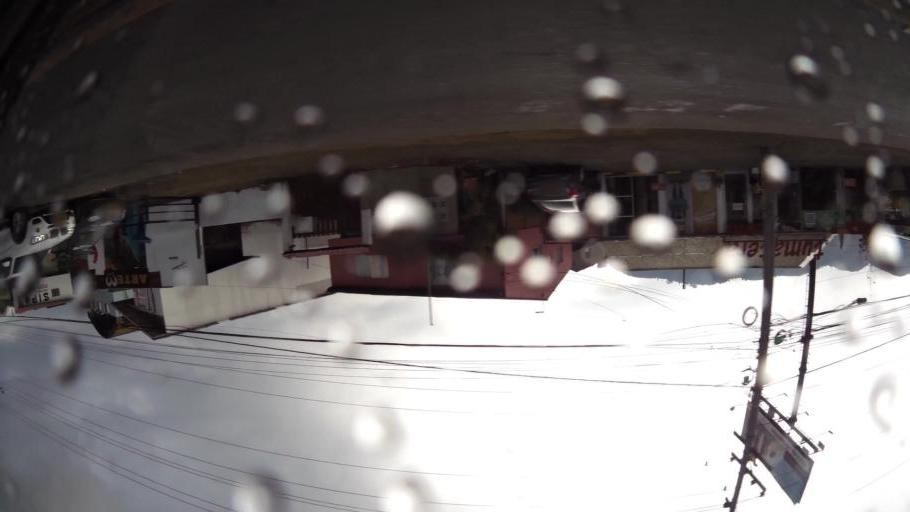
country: CO
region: Cundinamarca
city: Chia
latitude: 4.8538
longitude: -74.0700
